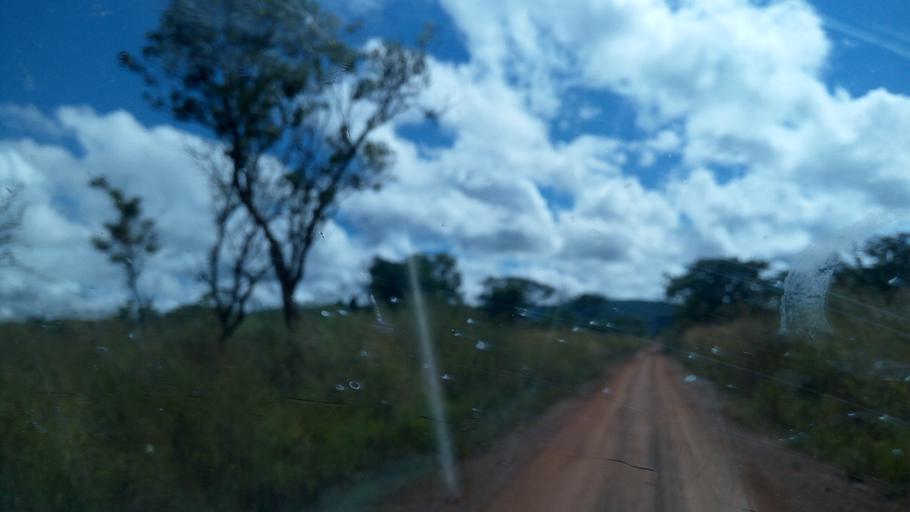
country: ZM
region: Northern
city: Kaputa
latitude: -8.2396
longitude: 29.0374
